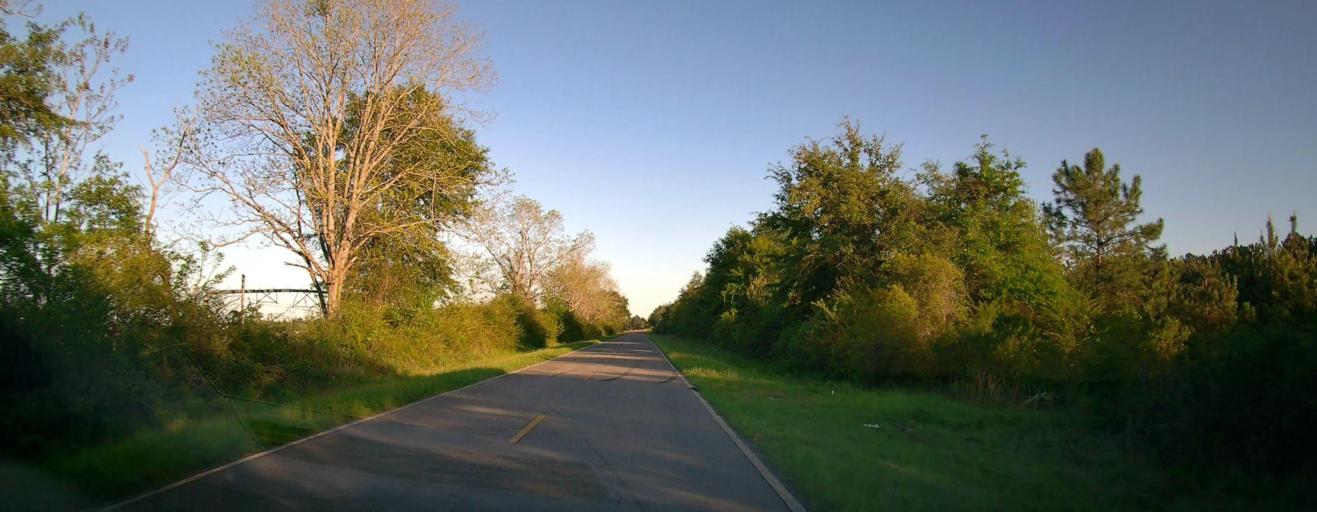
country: US
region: Georgia
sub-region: Ben Hill County
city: Fitzgerald
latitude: 31.6837
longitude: -83.2269
